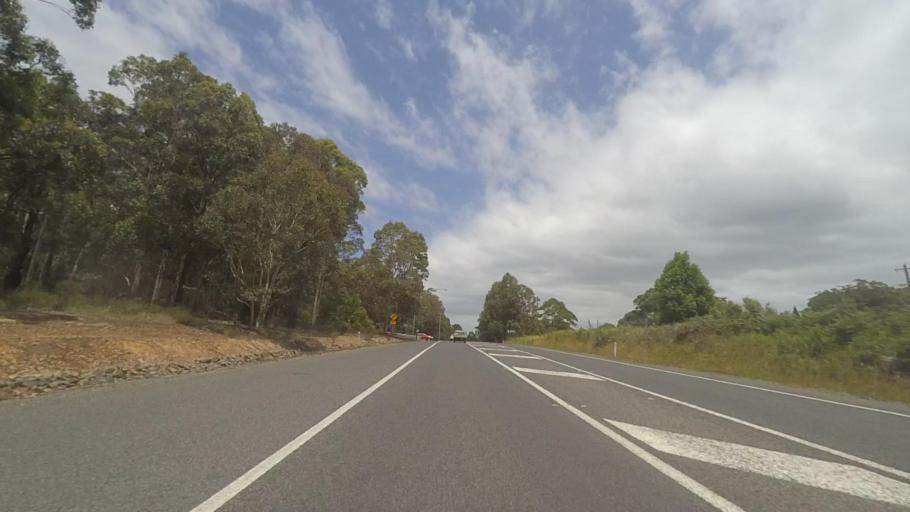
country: AU
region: New South Wales
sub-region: Shoalhaven Shire
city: Falls Creek
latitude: -35.0824
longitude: 150.5446
